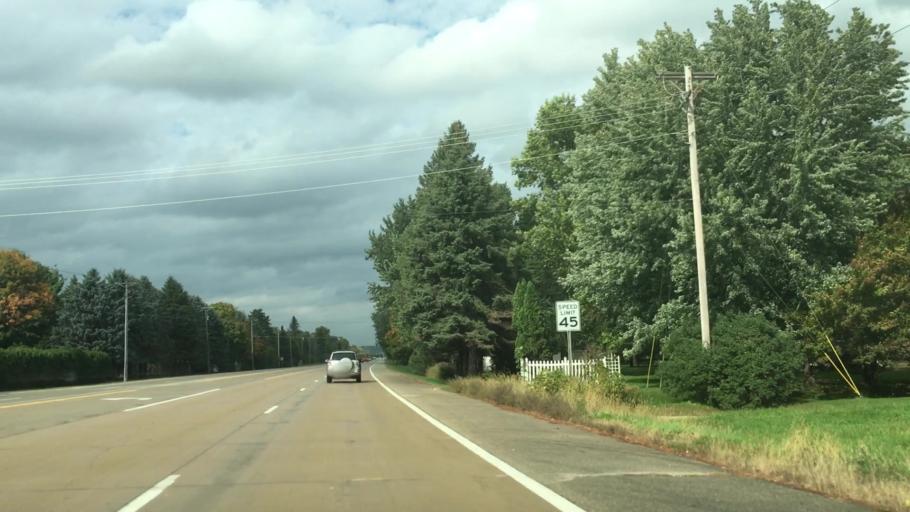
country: US
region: Minnesota
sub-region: Olmsted County
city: Rochester
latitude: 43.9780
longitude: -92.4398
